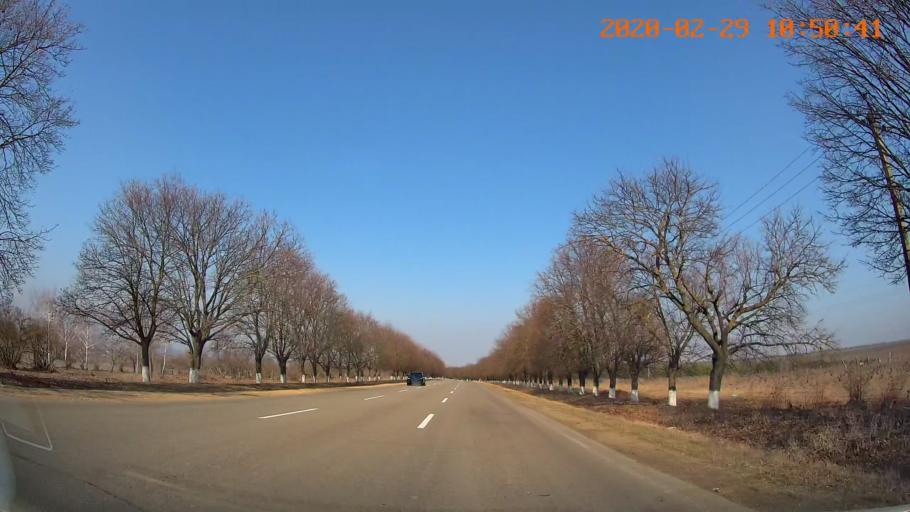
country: MD
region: Telenesti
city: Grigoriopol
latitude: 47.0855
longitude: 29.3730
